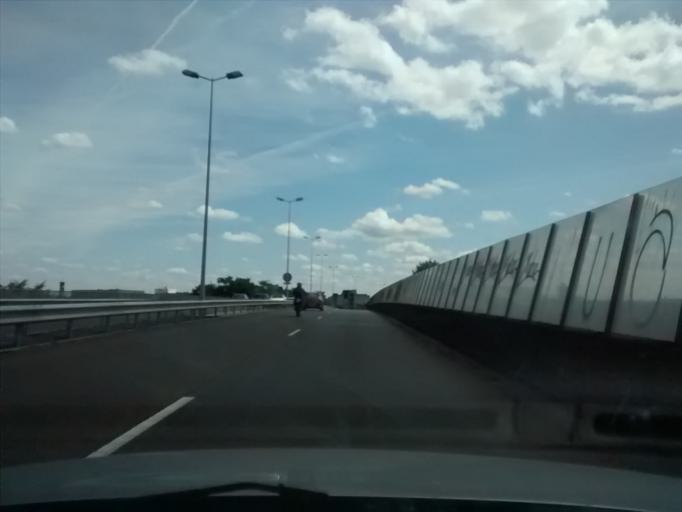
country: FR
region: Pays de la Loire
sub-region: Departement de la Sarthe
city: Le Mans
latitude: 47.9795
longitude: 0.2003
